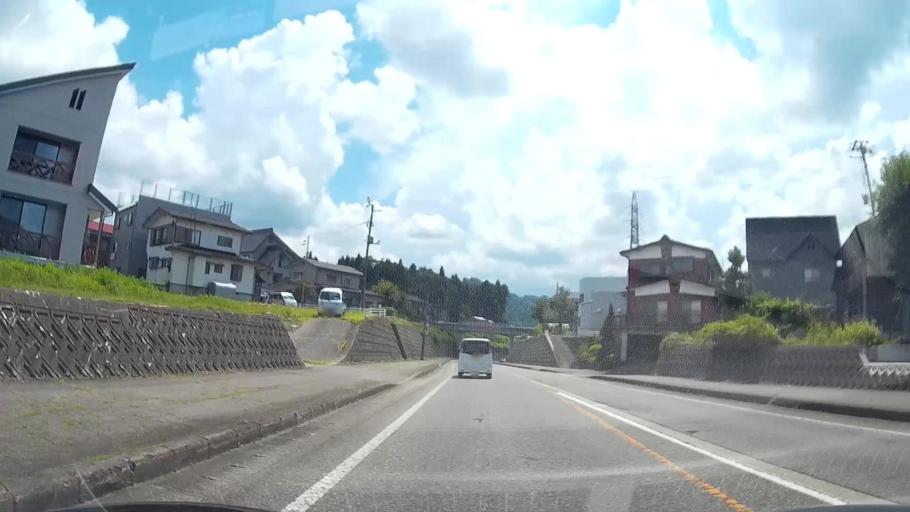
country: JP
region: Niigata
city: Tokamachi
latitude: 37.0190
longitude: 138.6556
